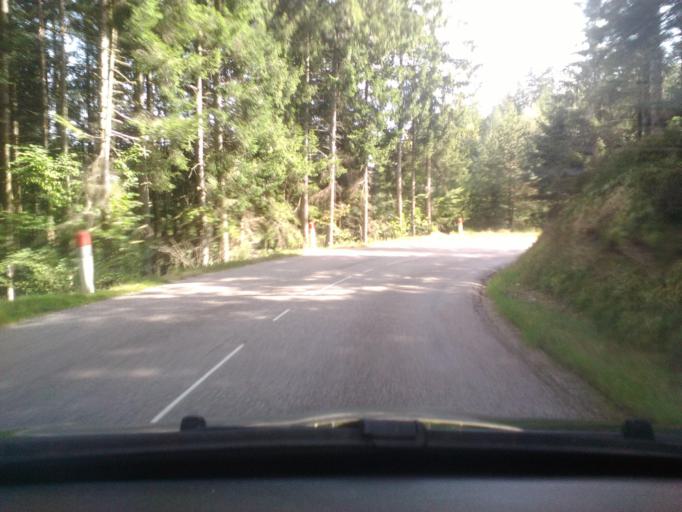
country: FR
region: Lorraine
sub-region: Departement des Vosges
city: Bruyeres
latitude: 48.2726
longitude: 6.7883
